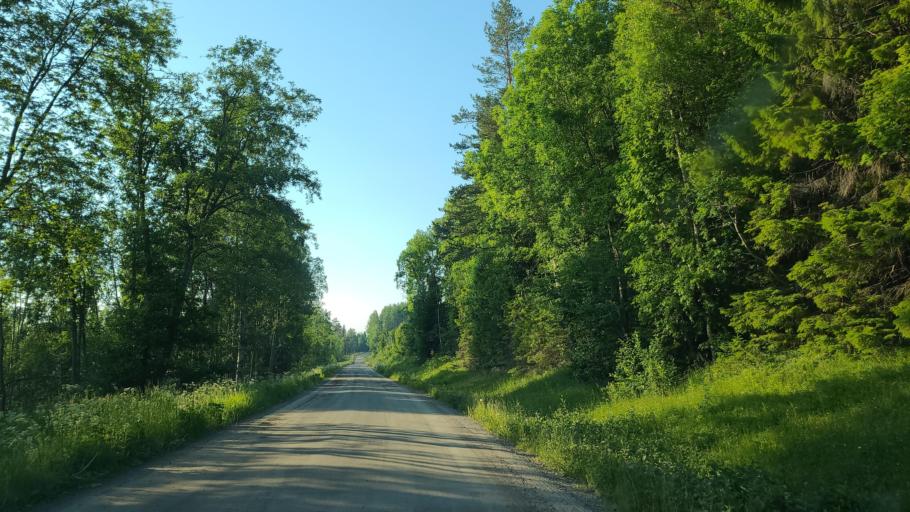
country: SE
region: Vaesterbotten
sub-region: Skelleftea Kommun
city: Burea
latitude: 64.3481
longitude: 21.3553
